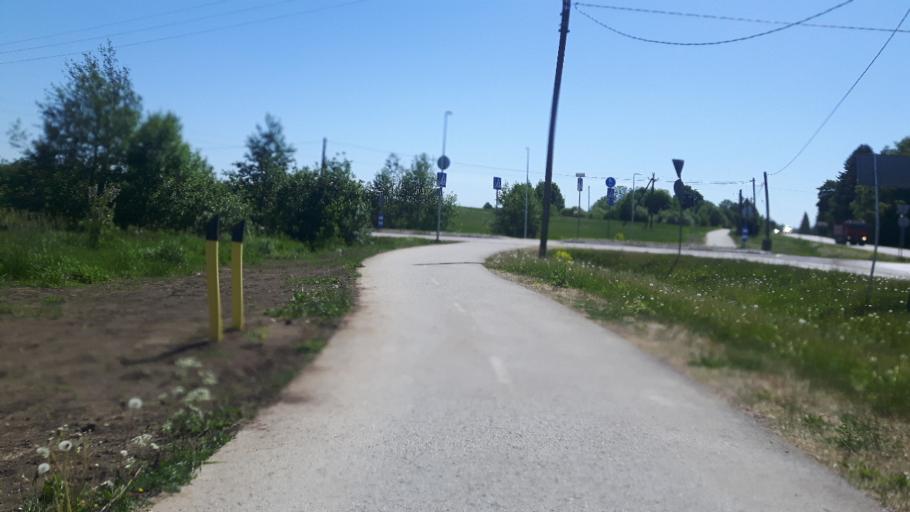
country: EE
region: Harju
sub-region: Saku vald
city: Saku
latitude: 59.2894
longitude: 24.6612
